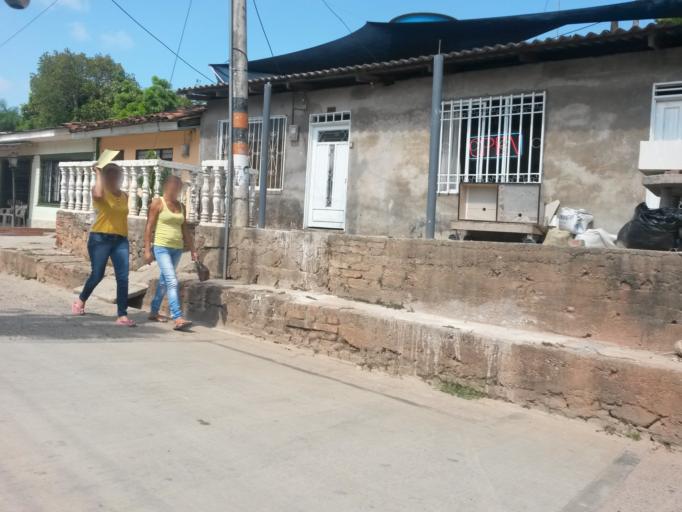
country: CO
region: Cauca
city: El Bordo
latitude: 2.1171
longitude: -76.9826
